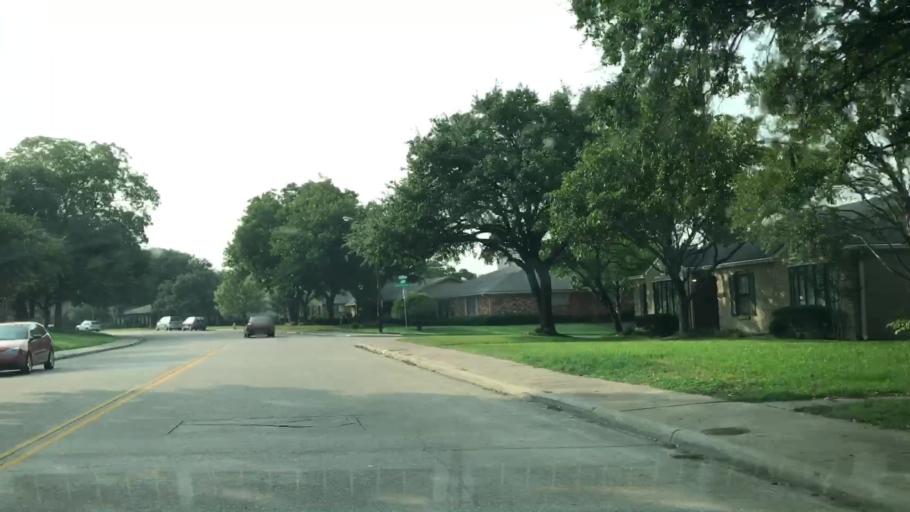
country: US
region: Texas
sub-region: Dallas County
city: Richardson
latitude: 32.9051
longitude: -96.7331
